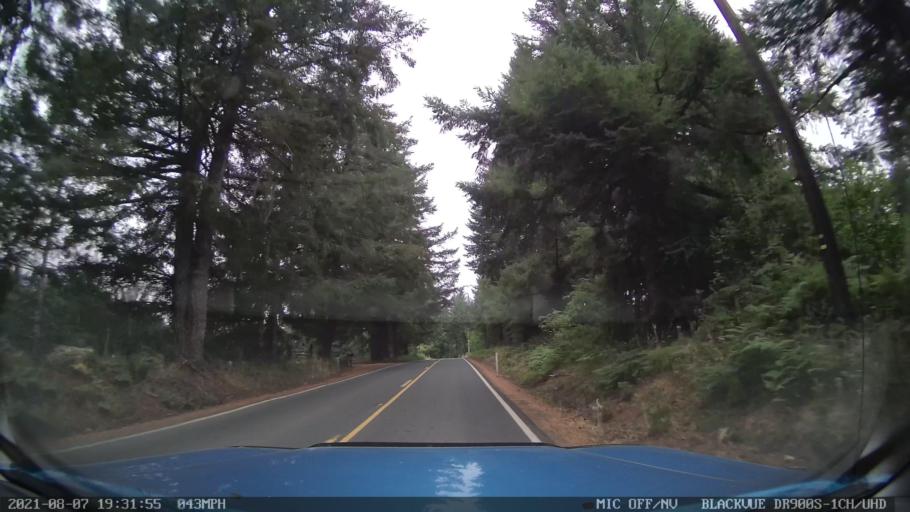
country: US
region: Oregon
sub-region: Linn County
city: Lyons
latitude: 44.8957
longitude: -122.6382
